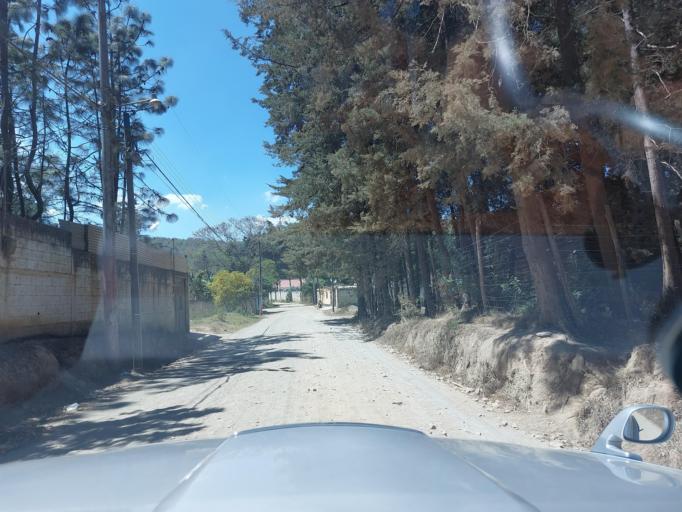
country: GT
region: Chimaltenango
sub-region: Municipio de Chimaltenango
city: Chimaltenango
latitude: 14.6551
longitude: -90.8269
